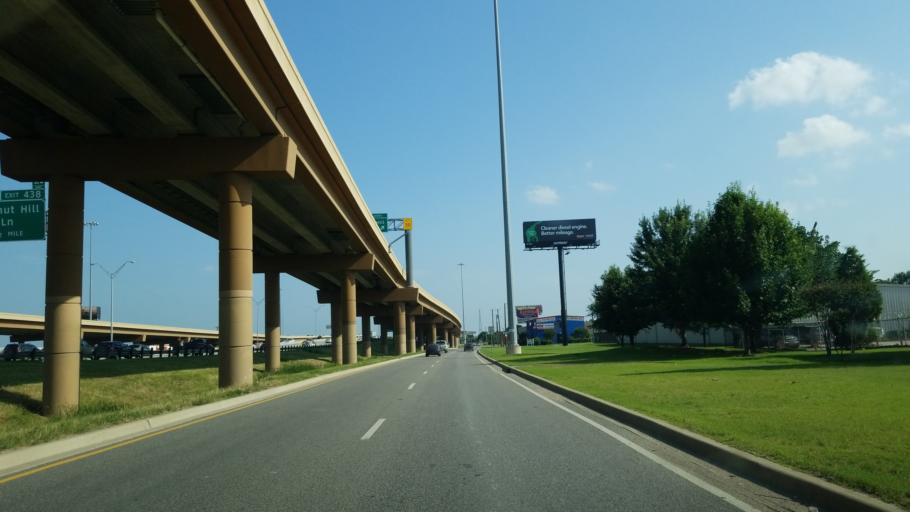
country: US
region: Texas
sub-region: Dallas County
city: Farmers Branch
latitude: 32.8912
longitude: -96.8985
